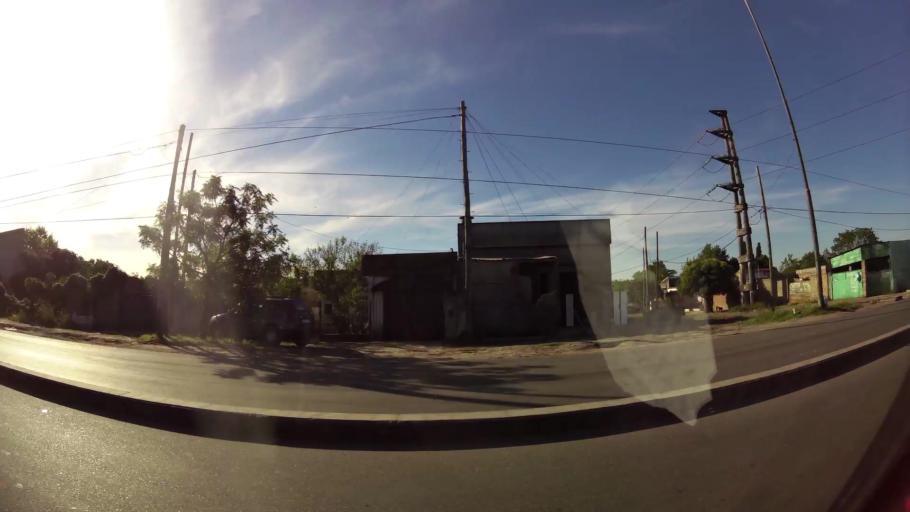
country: AR
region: Buenos Aires
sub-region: Partido de Almirante Brown
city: Adrogue
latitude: -34.8097
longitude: -58.3451
